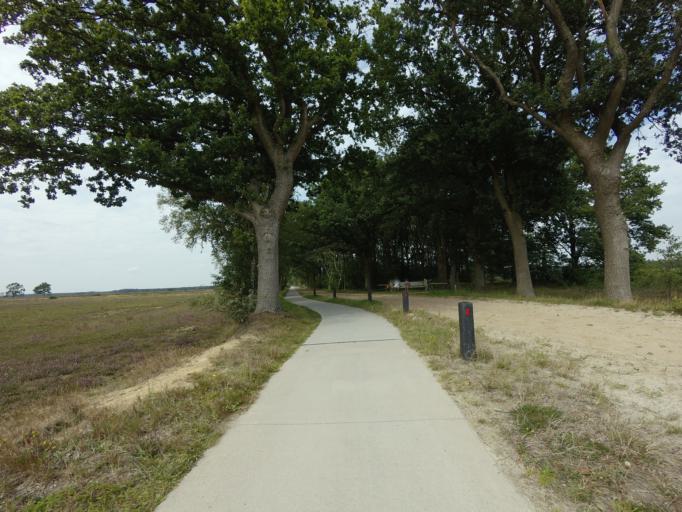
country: NL
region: Drenthe
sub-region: Gemeente Westerveld
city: Dwingeloo
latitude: 52.8049
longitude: 6.4136
